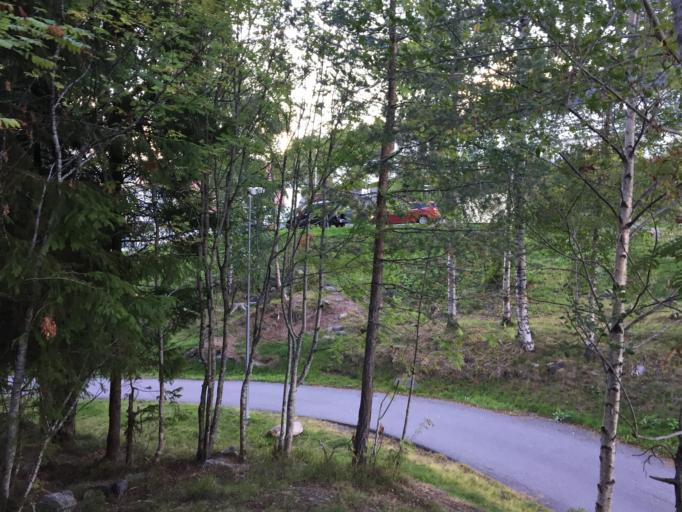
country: NO
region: Akershus
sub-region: Raelingen
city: Fjerdingby
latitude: 59.9315
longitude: 11.0427
